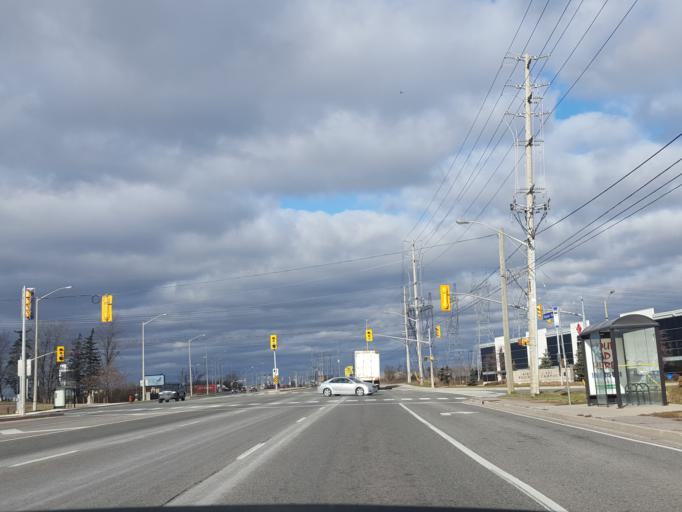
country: CA
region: Ontario
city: Brampton
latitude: 43.7202
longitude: -79.6643
